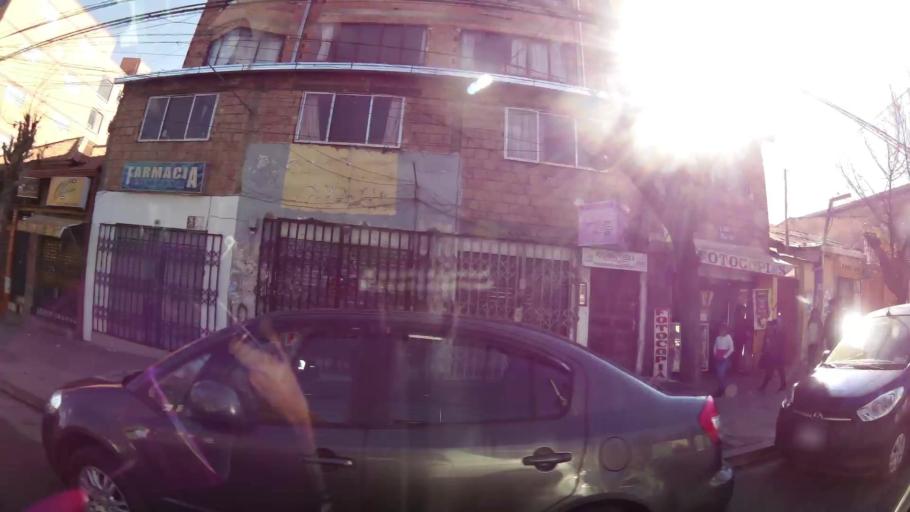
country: BO
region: La Paz
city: La Paz
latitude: -16.5066
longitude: -68.1200
